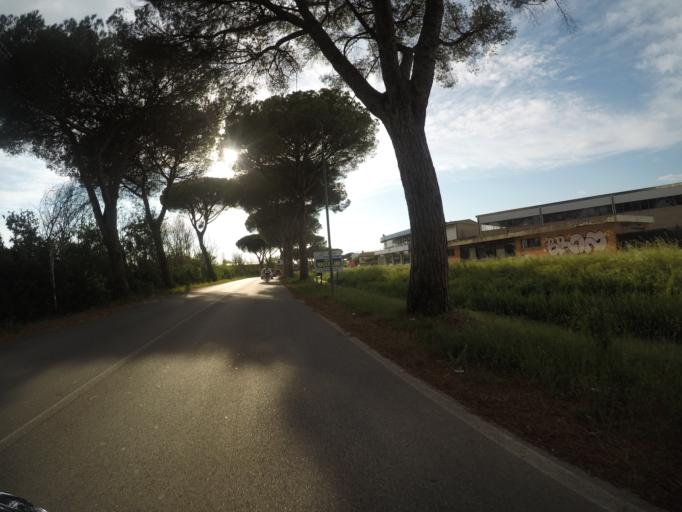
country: IT
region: Tuscany
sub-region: Province of Pisa
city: Madonna dell'Acqua
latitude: 43.7400
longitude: 10.3795
